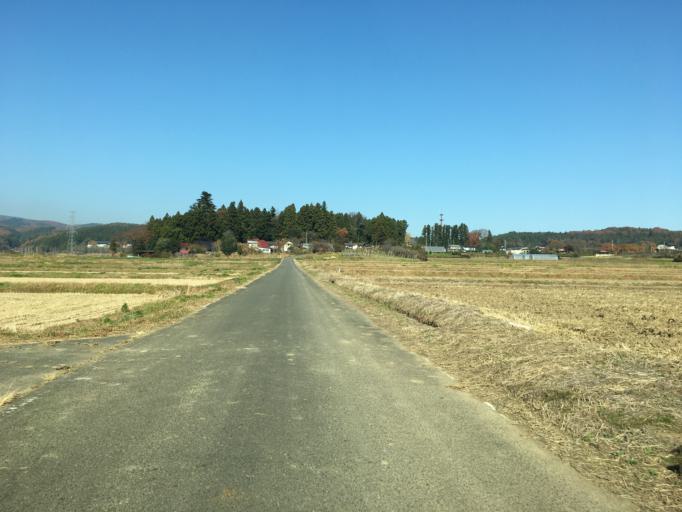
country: JP
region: Fukushima
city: Nihommatsu
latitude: 37.5761
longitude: 140.3903
